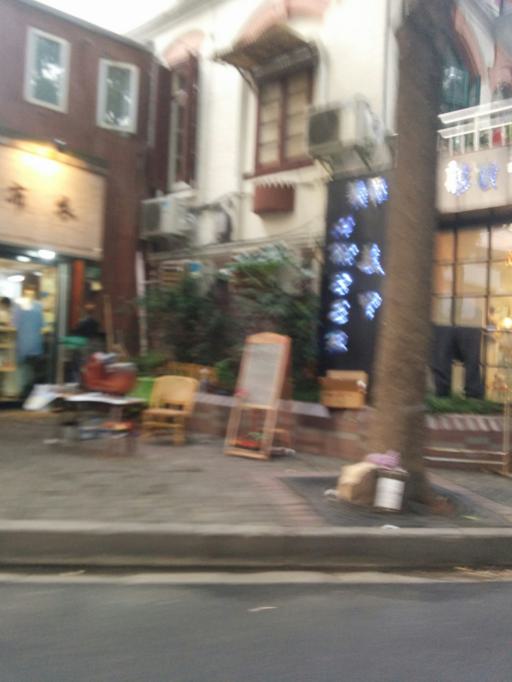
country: CN
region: Shanghai Shi
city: Shanghai
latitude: 31.2318
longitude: 121.4528
